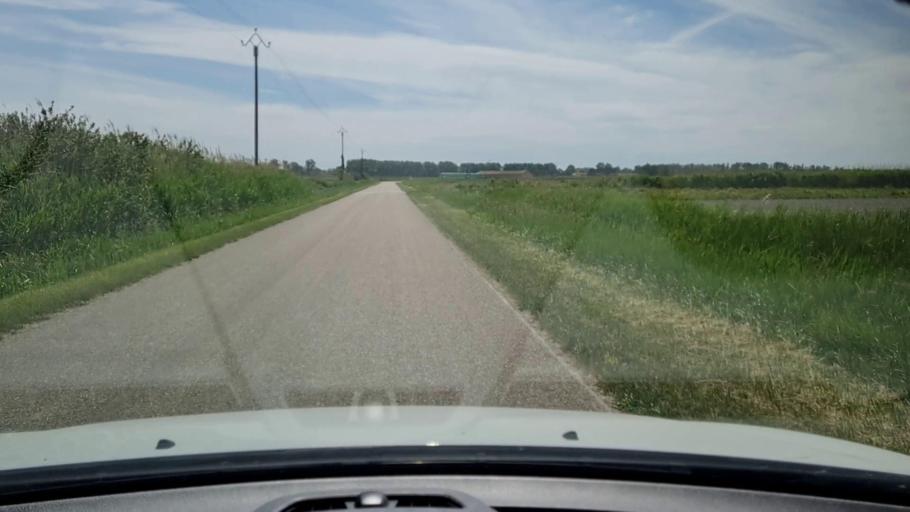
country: FR
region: Languedoc-Roussillon
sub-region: Departement du Gard
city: Saint-Gilles
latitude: 43.5917
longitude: 4.4538
